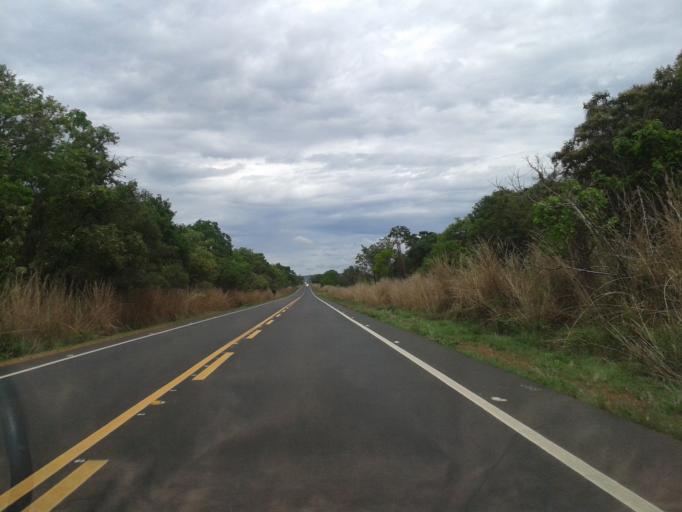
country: BR
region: Goias
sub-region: Caldas Novas
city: Caldas Novas
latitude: -17.8611
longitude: -48.6412
